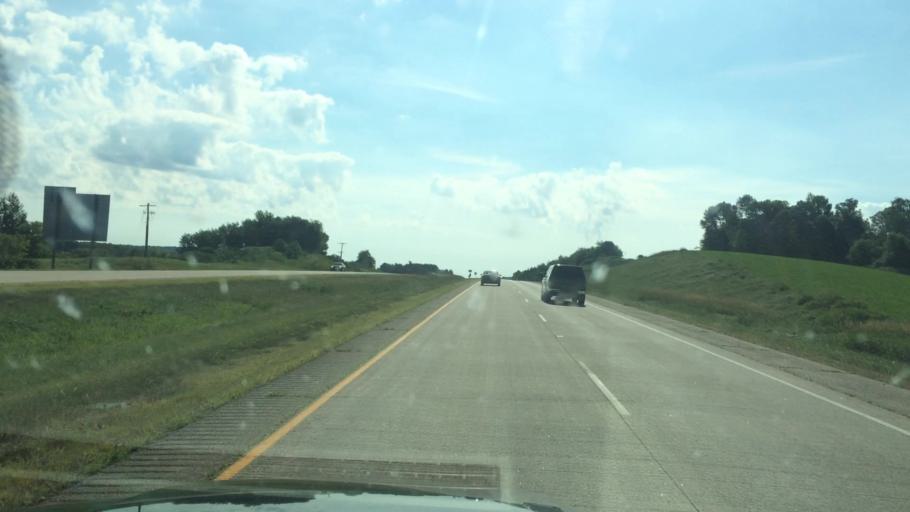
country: US
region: Wisconsin
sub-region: Shawano County
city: Wittenberg
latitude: 44.8260
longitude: -89.1077
